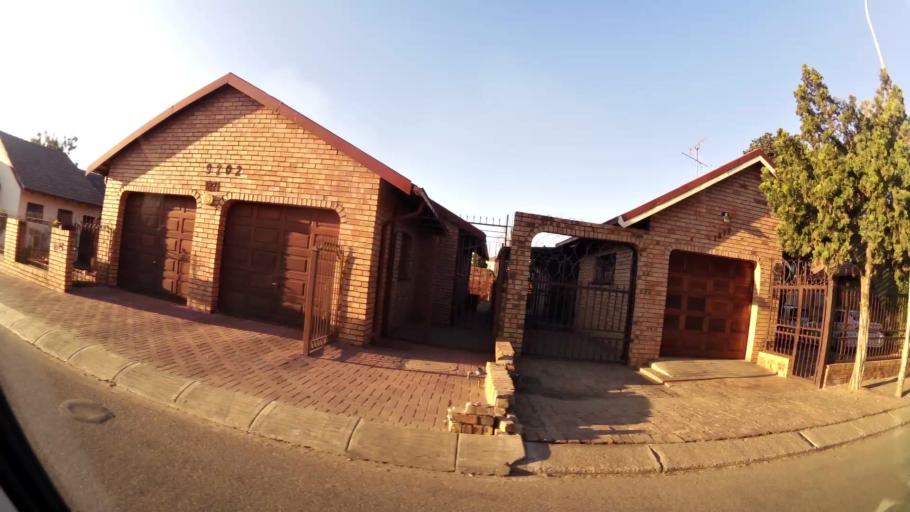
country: ZA
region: Gauteng
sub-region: City of Tshwane Metropolitan Municipality
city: Cullinan
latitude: -25.7249
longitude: 28.3916
